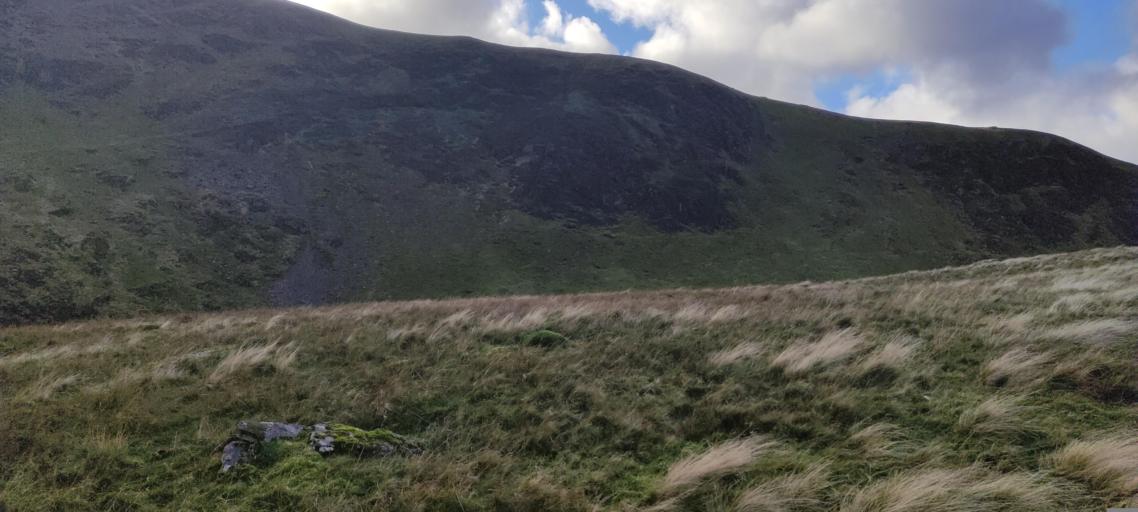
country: GB
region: England
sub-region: Cumbria
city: Keswick
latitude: 54.6737
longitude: -3.0283
